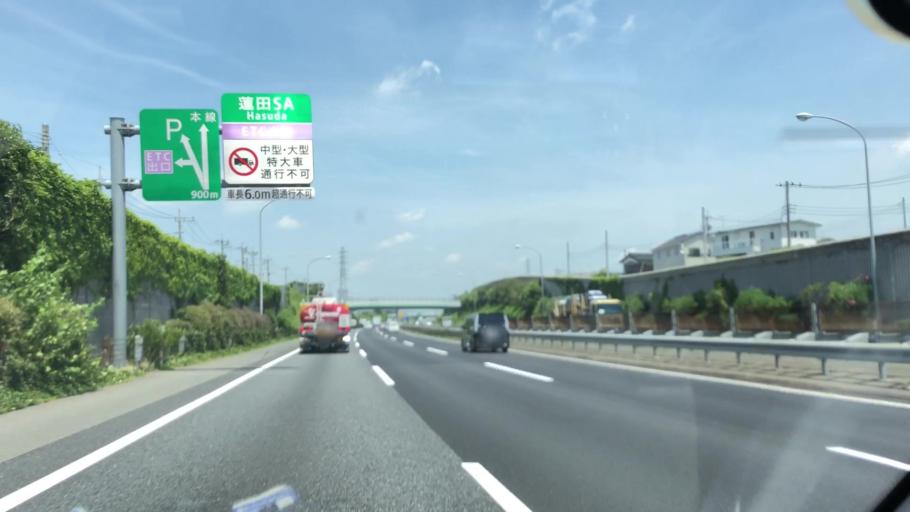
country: JP
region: Saitama
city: Hasuda
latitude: 35.9892
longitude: 139.6638
